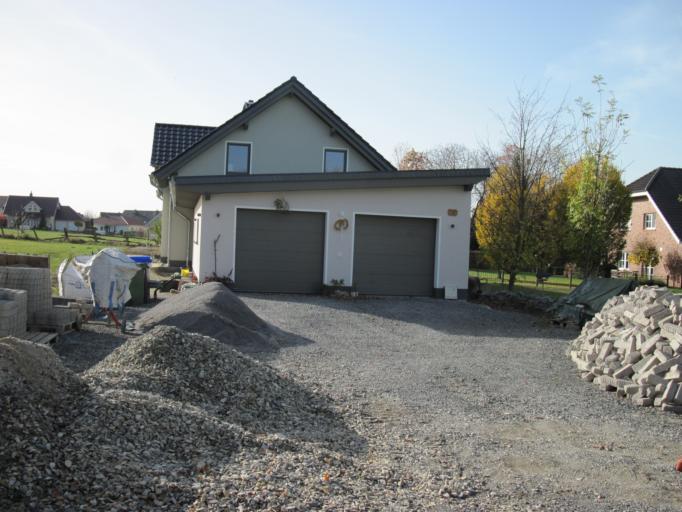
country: DE
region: North Rhine-Westphalia
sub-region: Regierungsbezirk Detmold
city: Salzkotten
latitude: 51.6066
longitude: 8.6650
